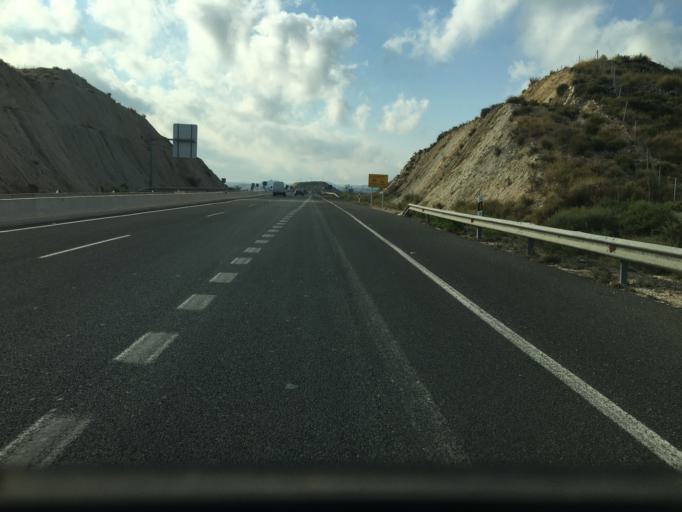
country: ES
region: Murcia
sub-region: Murcia
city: Beniel
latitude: 38.0003
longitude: -1.0107
